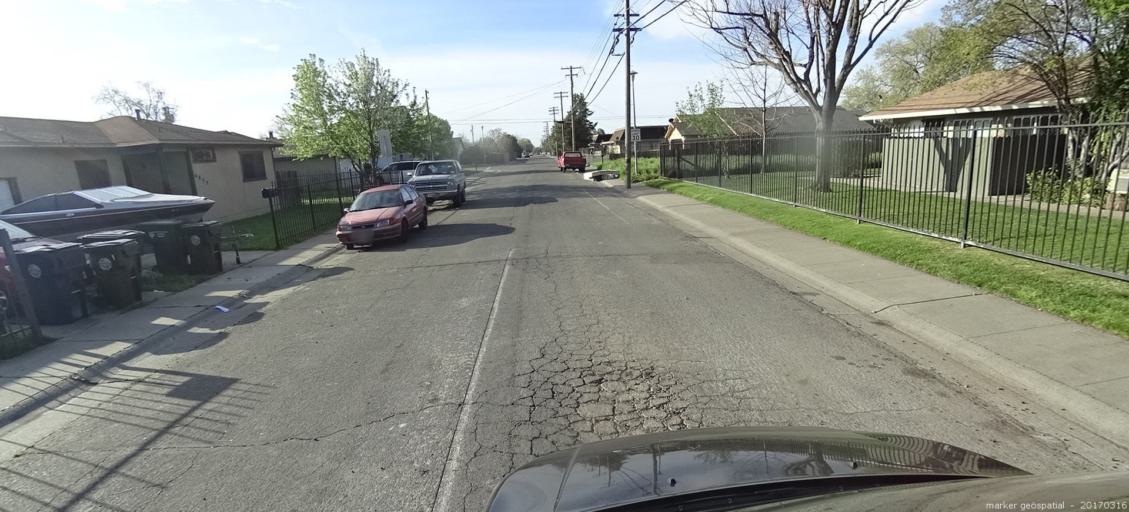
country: US
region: California
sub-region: Sacramento County
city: Parkway
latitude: 38.5021
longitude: -121.4792
